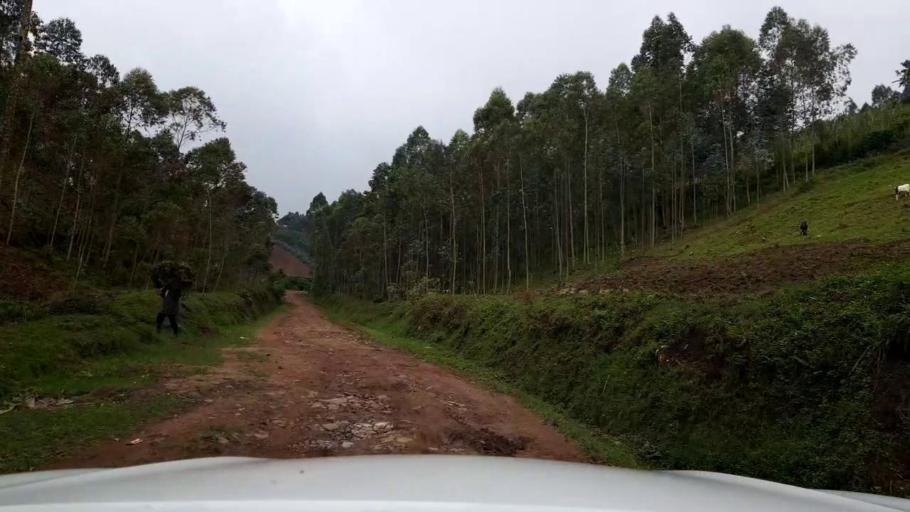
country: RW
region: Northern Province
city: Musanze
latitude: -1.6069
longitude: 29.7673
